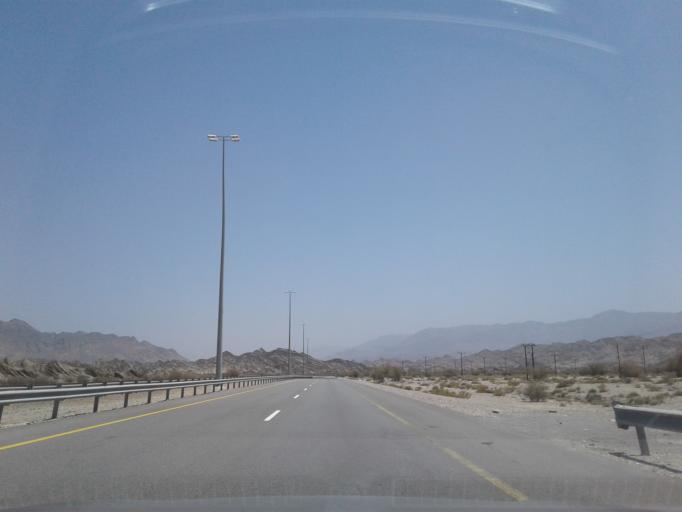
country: OM
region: Muhafazat Masqat
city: Muscat
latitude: 23.3393
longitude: 58.7013
